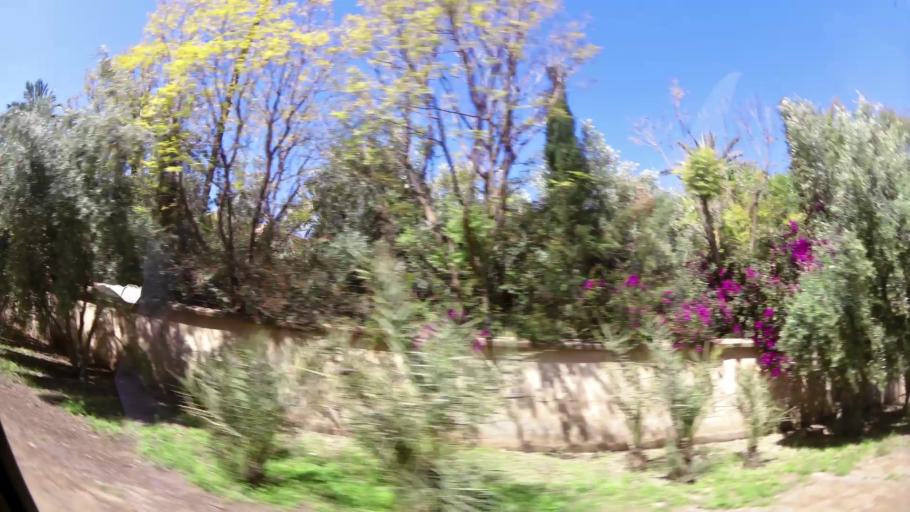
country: MA
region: Marrakech-Tensift-Al Haouz
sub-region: Marrakech
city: Marrakesh
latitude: 31.6719
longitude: -7.9841
